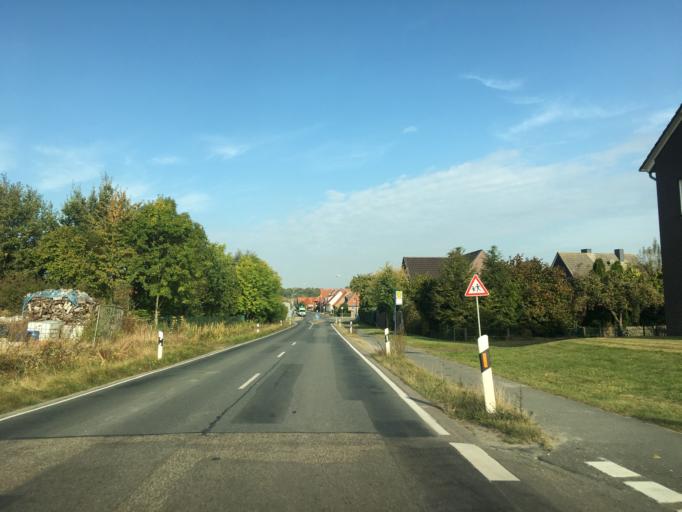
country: DE
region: North Rhine-Westphalia
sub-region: Regierungsbezirk Munster
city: Nordwalde
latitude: 52.0783
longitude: 7.4785
